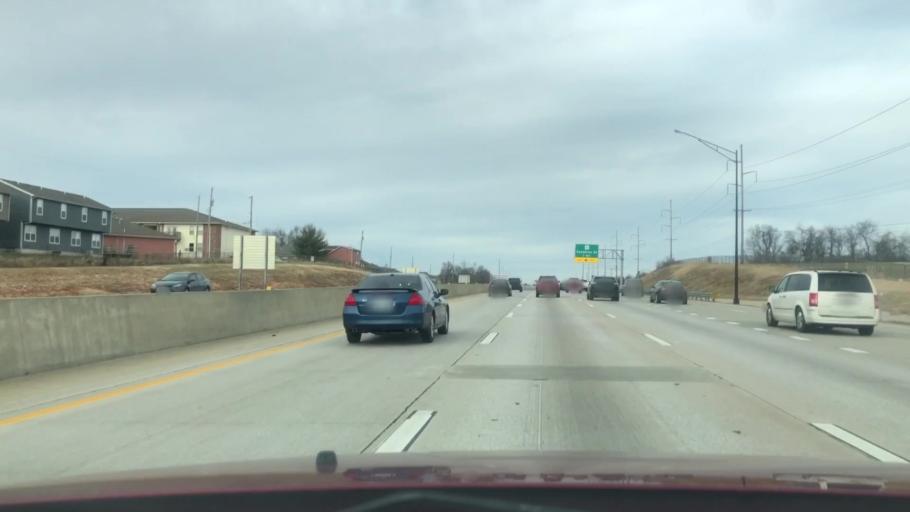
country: US
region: Missouri
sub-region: Greene County
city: Springfield
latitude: 37.1619
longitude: -93.2243
